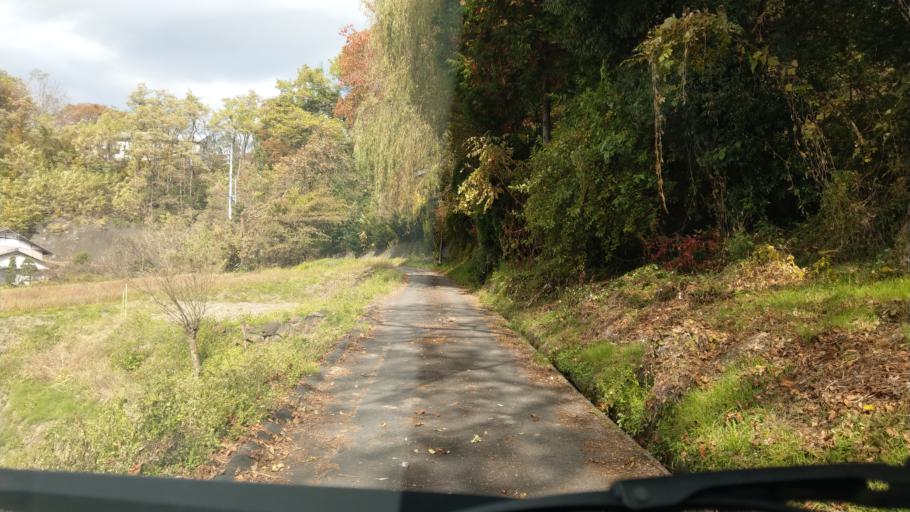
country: JP
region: Nagano
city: Komoro
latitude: 36.3290
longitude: 138.4139
